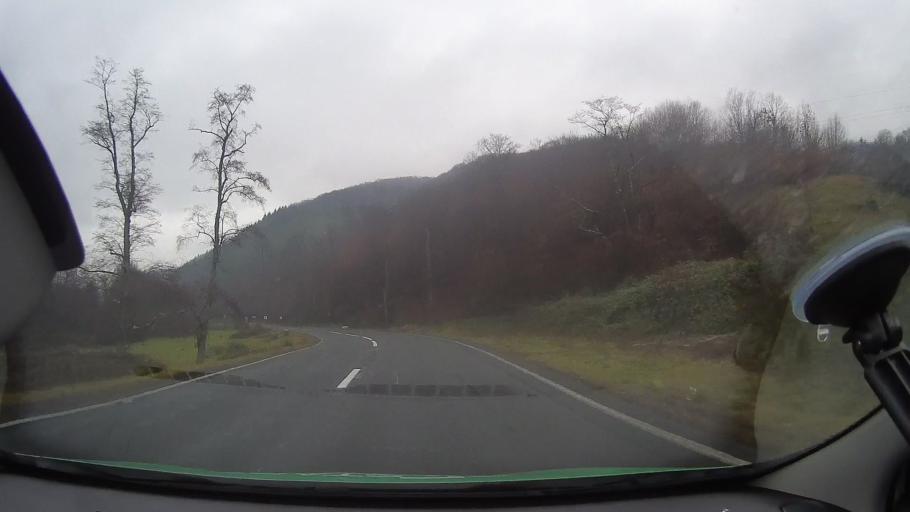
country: RO
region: Arad
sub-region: Comuna Plescuta
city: Plescuta
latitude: 46.3008
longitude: 22.4552
